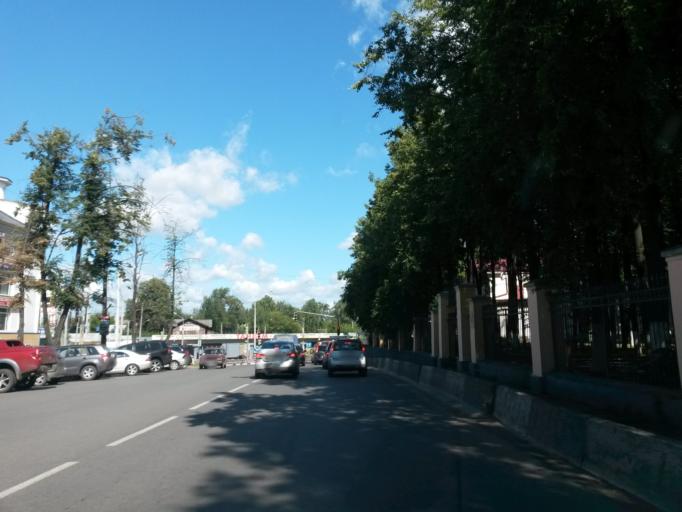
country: RU
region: Jaroslavl
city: Yaroslavl
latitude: 57.6007
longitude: 39.8778
